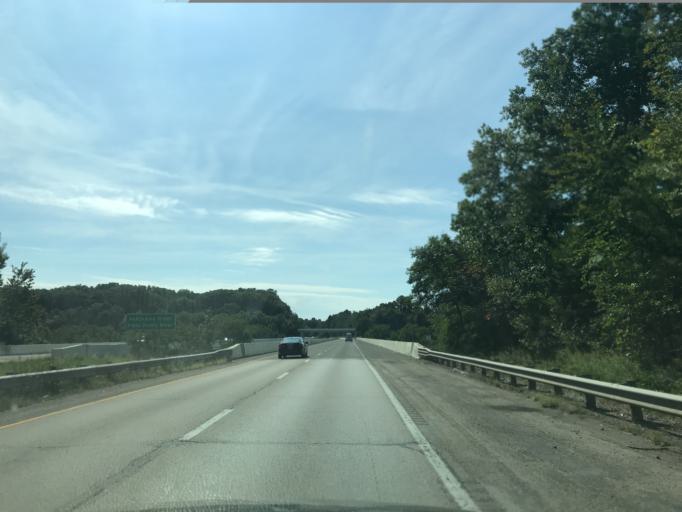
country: US
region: Ohio
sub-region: Ashtabula County
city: Edgewood
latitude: 41.8557
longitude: -80.7662
